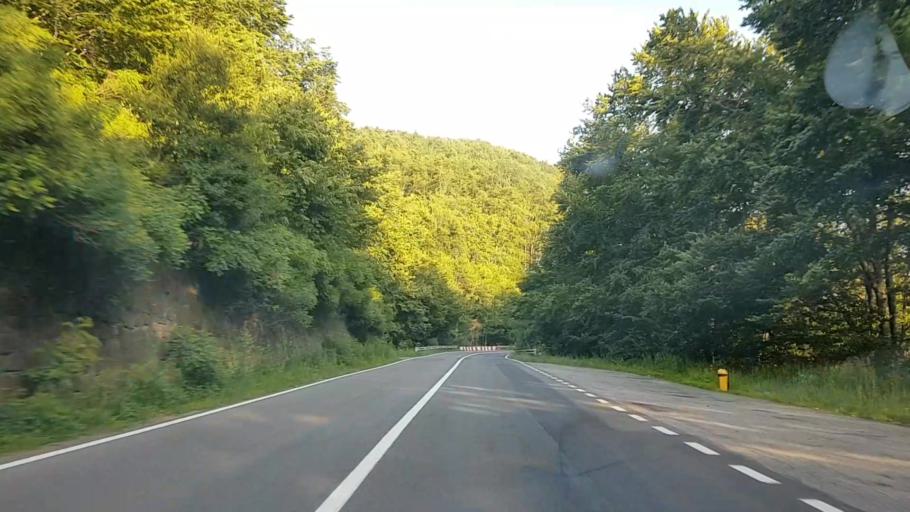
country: RO
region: Harghita
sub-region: Comuna Corund
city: Corund
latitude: 46.4475
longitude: 25.2271
